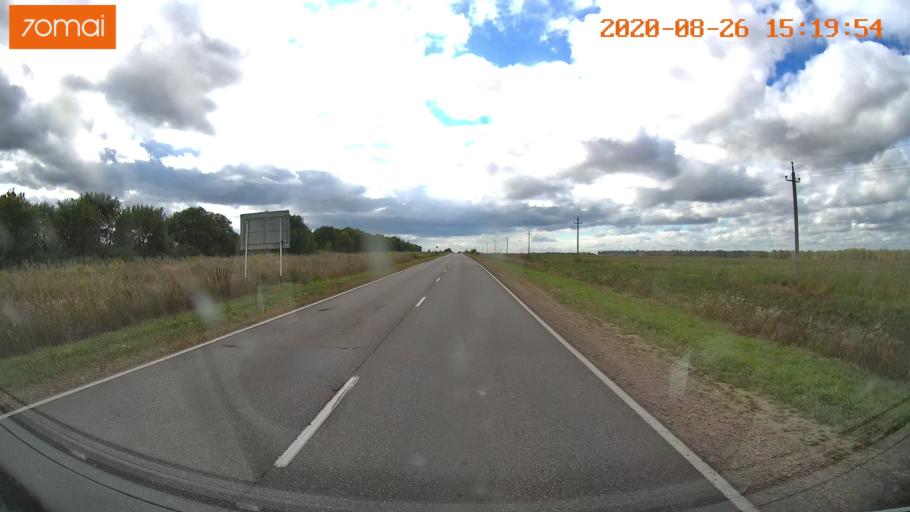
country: RU
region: Tula
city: Severo-Zadonsk
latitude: 54.1420
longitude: 38.5088
